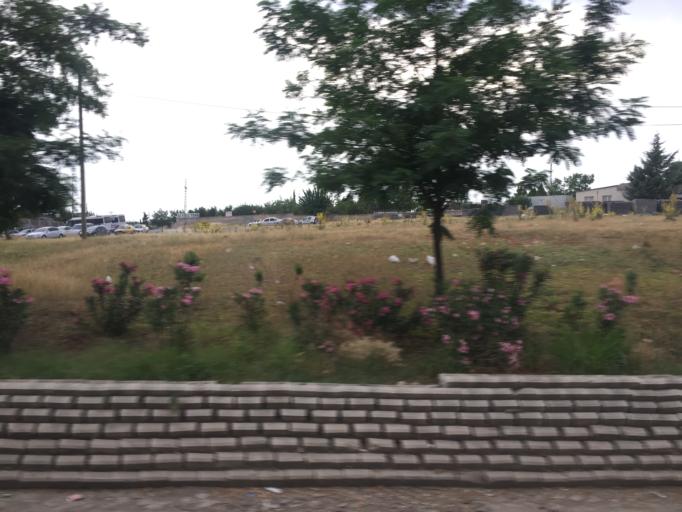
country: TR
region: Gaziantep
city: Gaziantep
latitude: 37.0222
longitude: 37.4284
